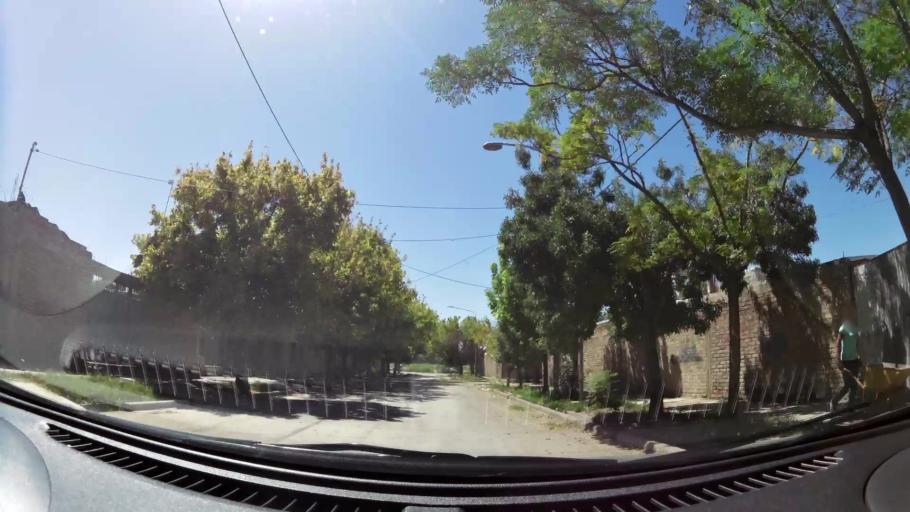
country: AR
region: Mendoza
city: Villa Nueva
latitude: -32.8738
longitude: -68.7984
